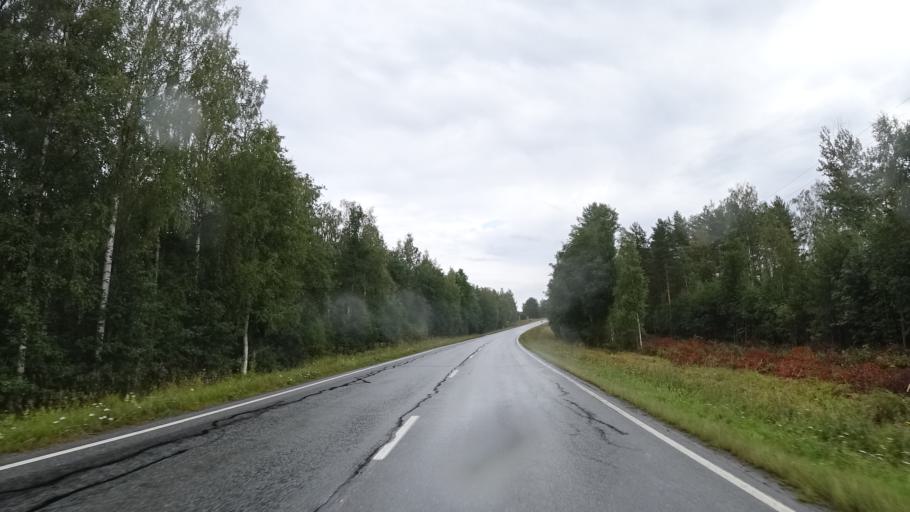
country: FI
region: North Karelia
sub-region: Keski-Karjala
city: Raeaekkylae
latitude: 62.0452
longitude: 29.5561
